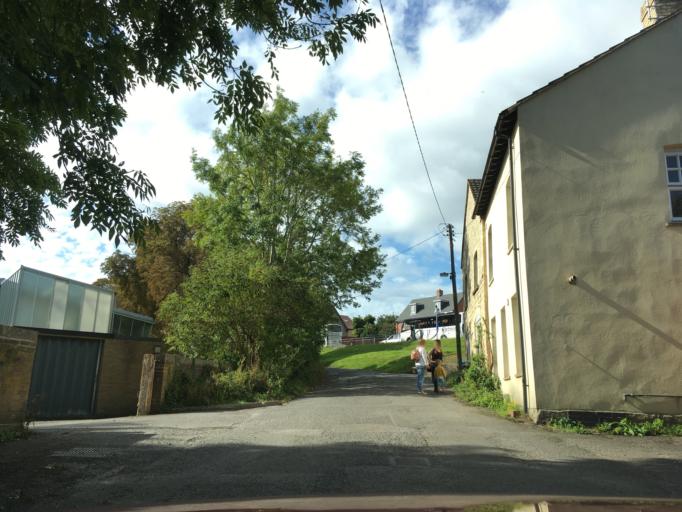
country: GB
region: England
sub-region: Gloucestershire
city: Stroud
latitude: 51.7446
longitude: -2.2292
